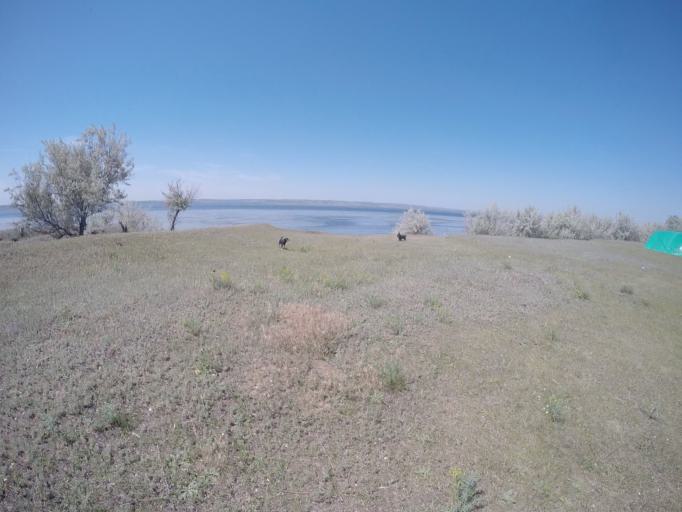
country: RU
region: Saratov
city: Krasnoarmeysk
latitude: 51.1659
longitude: 45.9040
